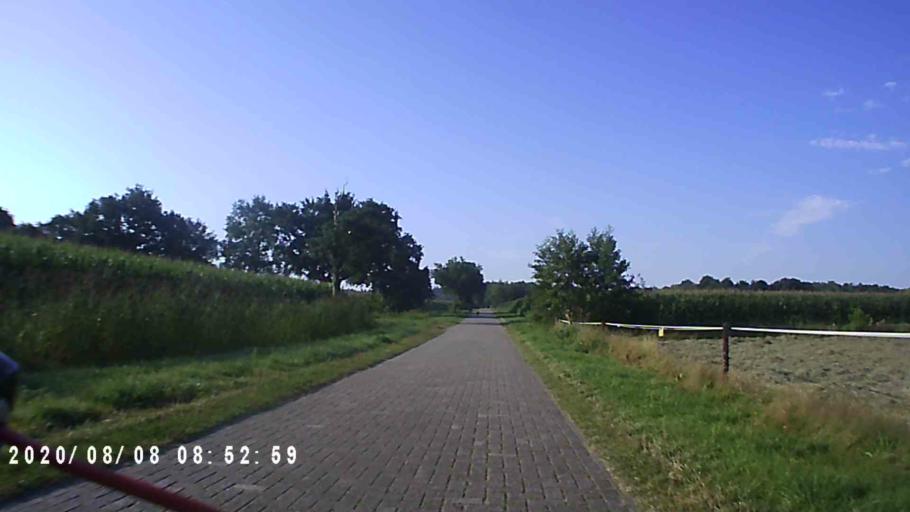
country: NL
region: Groningen
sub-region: Gemeente Leek
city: Leek
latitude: 53.0631
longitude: 6.3260
